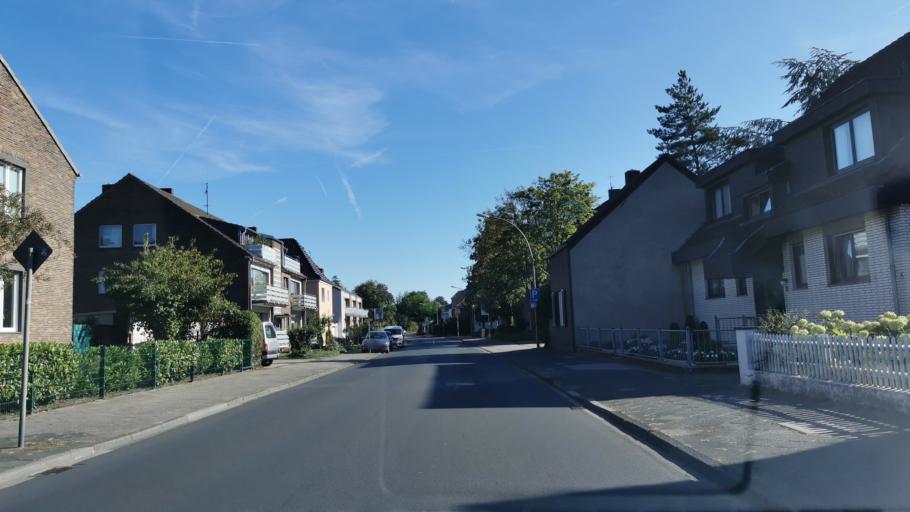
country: DE
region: North Rhine-Westphalia
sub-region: Regierungsbezirk Dusseldorf
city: Meerbusch
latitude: 51.2540
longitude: 6.6942
